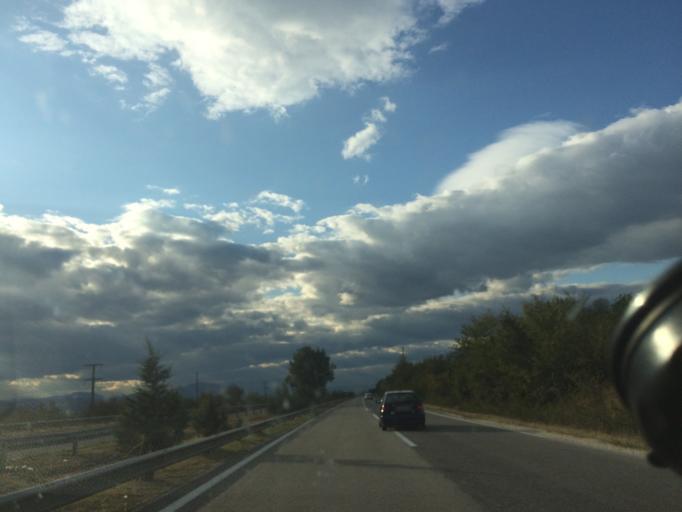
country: MK
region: Petrovec
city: Petrovec
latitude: 41.8960
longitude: 21.6702
